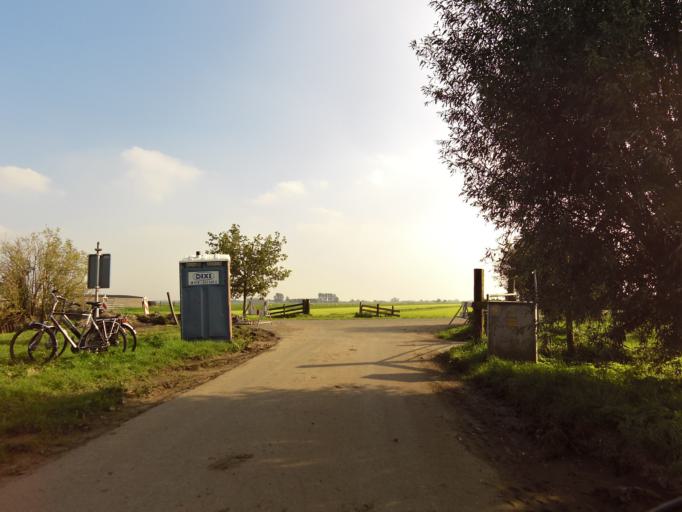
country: NL
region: South Holland
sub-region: Gemeente Leiderdorp
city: Leiderdorp
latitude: 52.1200
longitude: 4.5362
